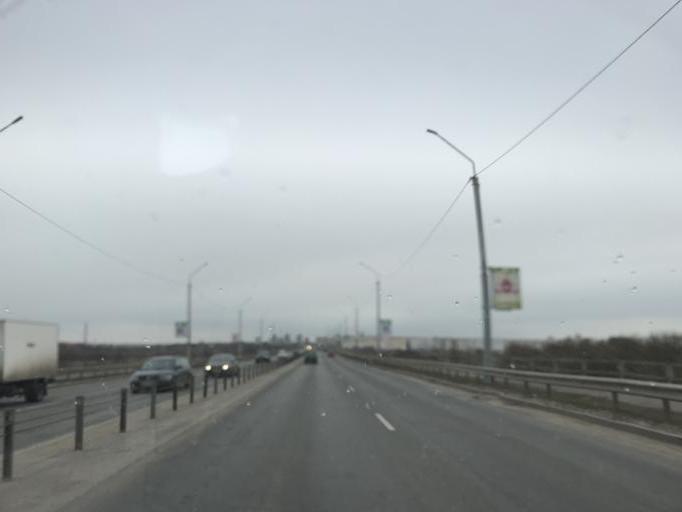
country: BY
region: Mogilev
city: Mahilyow
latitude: 53.8974
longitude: 30.3710
